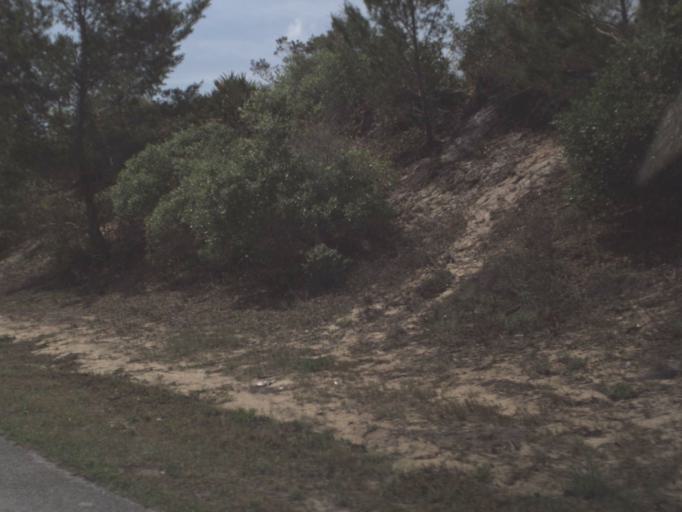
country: US
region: Florida
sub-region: Lake County
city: Astor
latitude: 29.2411
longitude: -81.6473
